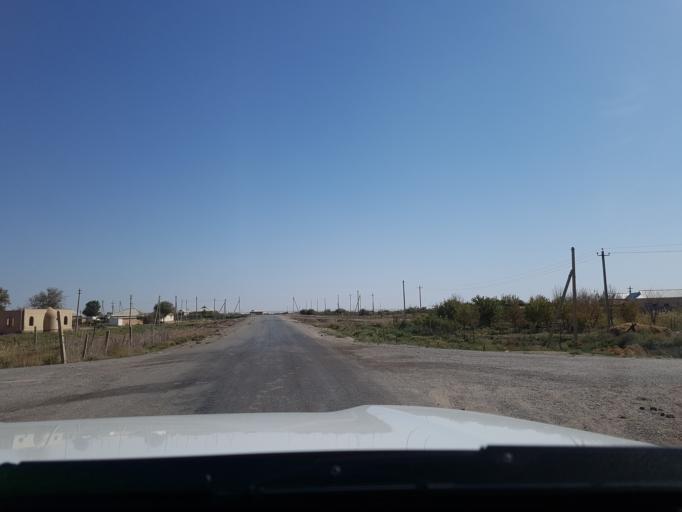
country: IR
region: Razavi Khorasan
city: Sarakhs
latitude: 36.5178
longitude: 61.2513
